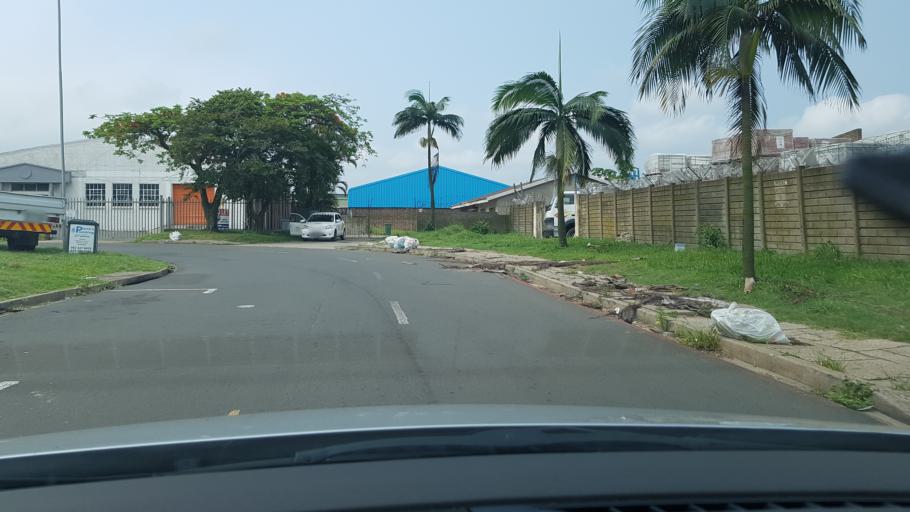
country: ZA
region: KwaZulu-Natal
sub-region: uThungulu District Municipality
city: Richards Bay
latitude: -28.7519
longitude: 32.0466
